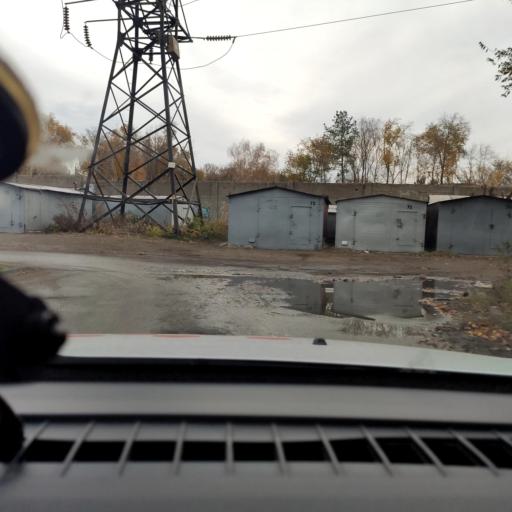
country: RU
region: Samara
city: Samara
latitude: 53.1910
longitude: 50.2217
